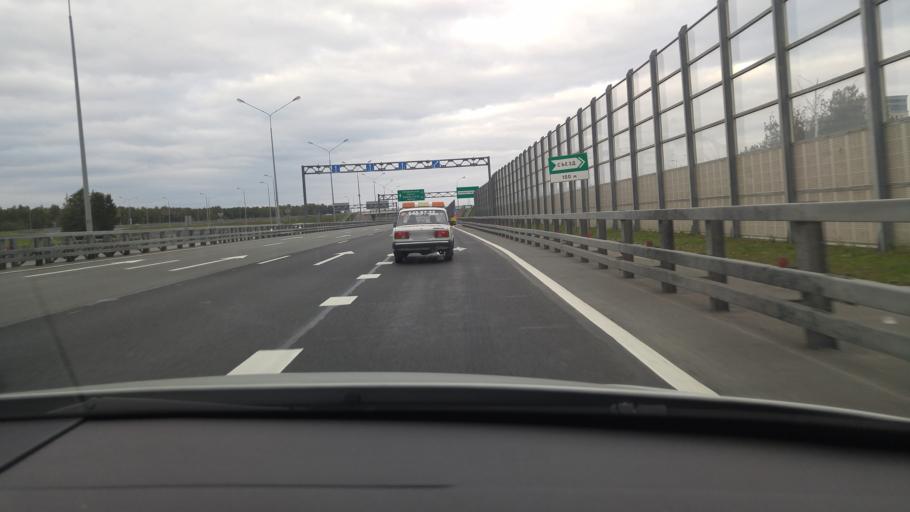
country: RU
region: St.-Petersburg
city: Kronshtadt
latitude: 60.0107
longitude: 29.7154
